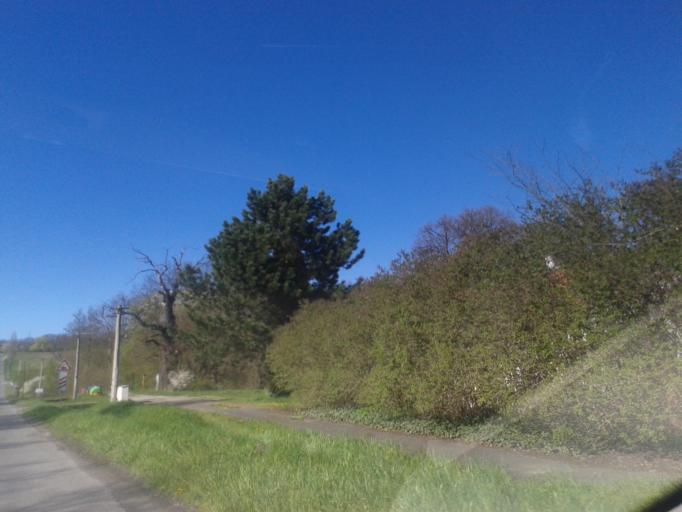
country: CZ
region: Central Bohemia
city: Revnice
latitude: 49.8864
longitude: 14.1495
